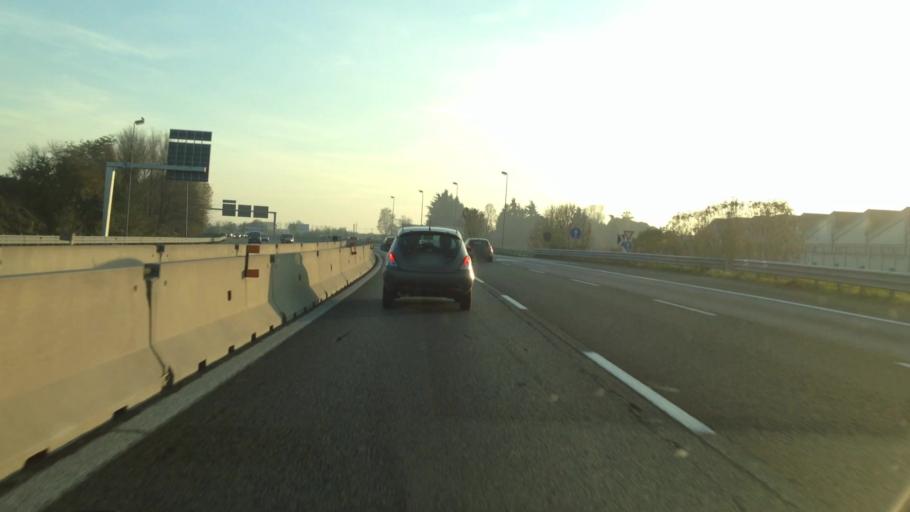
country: IT
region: Piedmont
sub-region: Provincia di Torino
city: Tetti Neirotti
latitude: 45.0630
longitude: 7.5435
